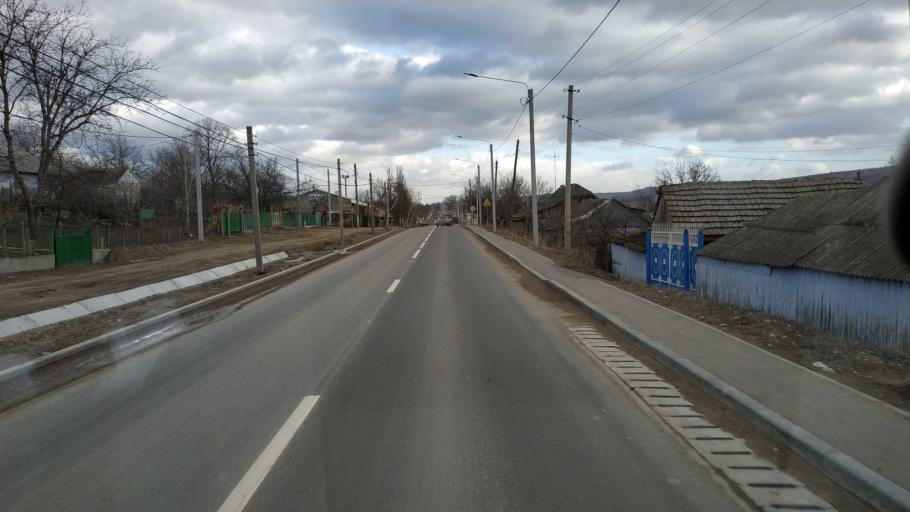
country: MD
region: Calarasi
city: Calarasi
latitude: 47.2826
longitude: 28.2051
